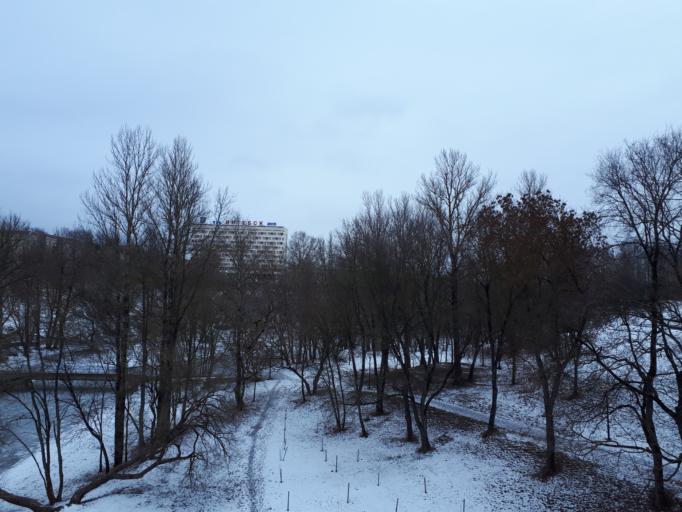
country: BY
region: Vitebsk
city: Vitebsk
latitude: 55.1950
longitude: 30.2089
